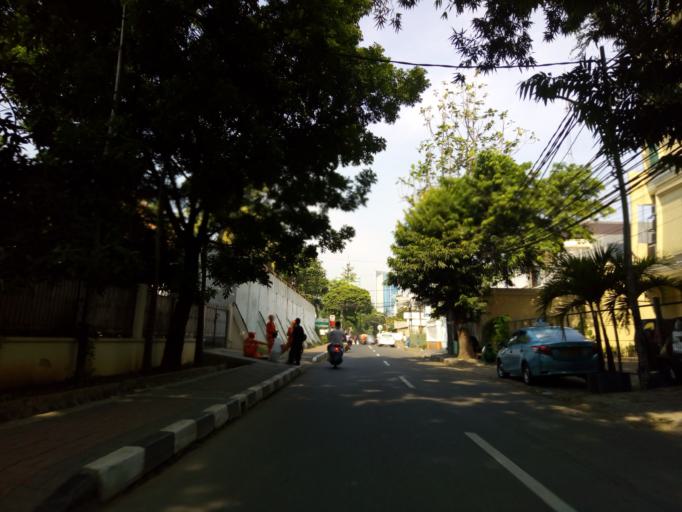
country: ID
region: Jakarta Raya
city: Jakarta
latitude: -6.2073
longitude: 106.8380
